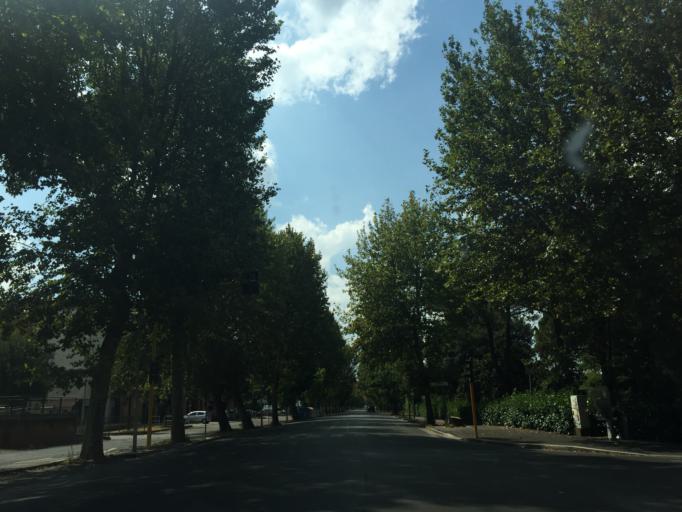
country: IT
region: Tuscany
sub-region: Province of Florence
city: Mantignano-Ugnano
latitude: 43.7936
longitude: 11.1794
